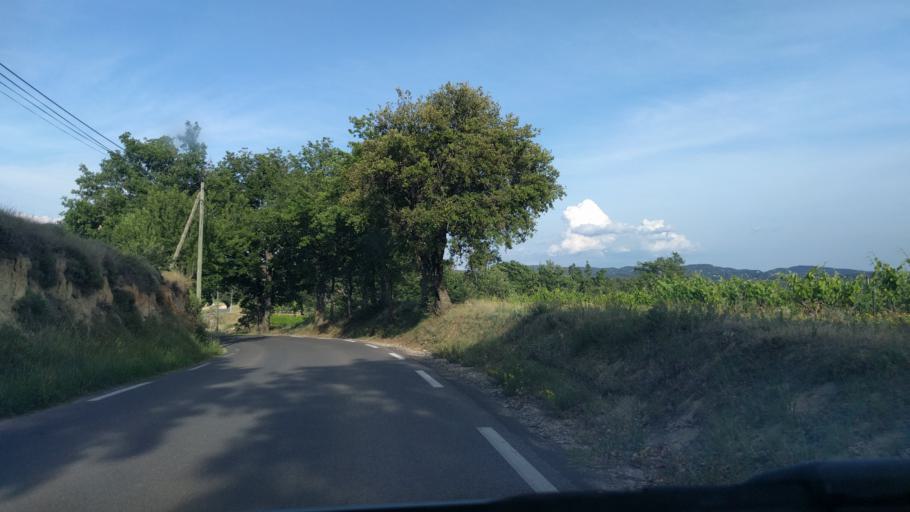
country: FR
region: Provence-Alpes-Cote d'Azur
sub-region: Departement du Vaucluse
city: Pertuis
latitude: 43.7336
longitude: 5.5236
